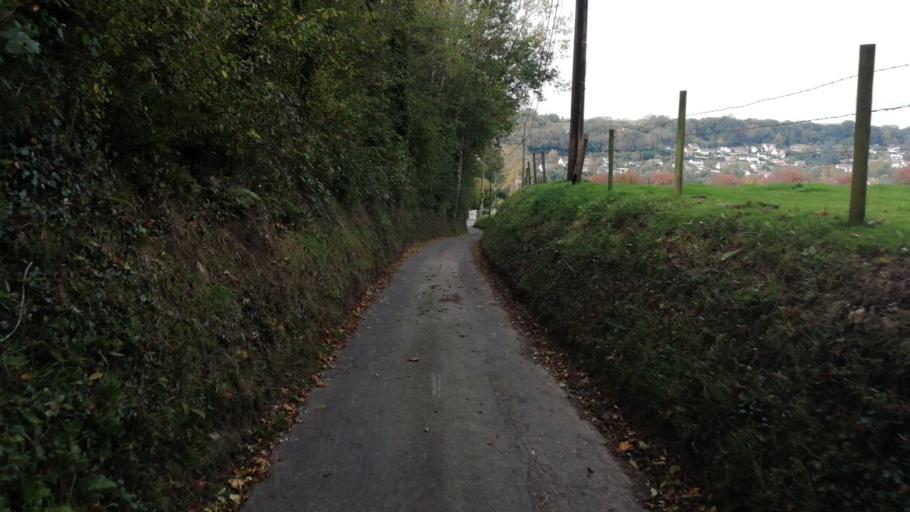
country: FR
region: Haute-Normandie
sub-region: Departement de la Seine-Maritime
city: Montivilliers
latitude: 49.5469
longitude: 0.2091
